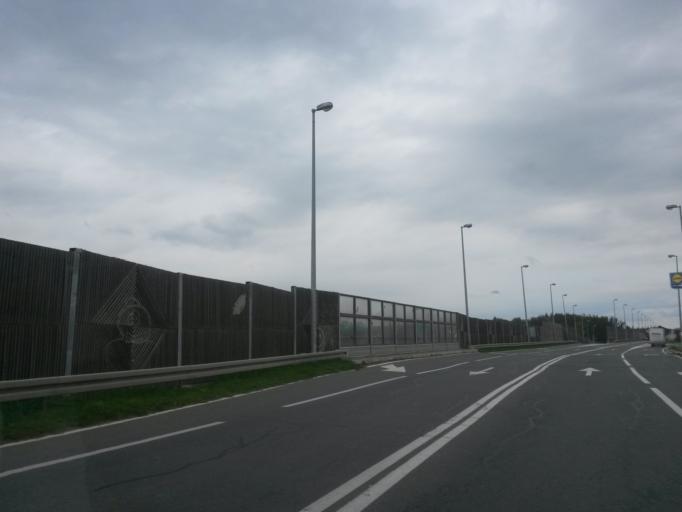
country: HR
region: Osjecko-Baranjska
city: Visnjevac
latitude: 45.5623
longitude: 18.6304
